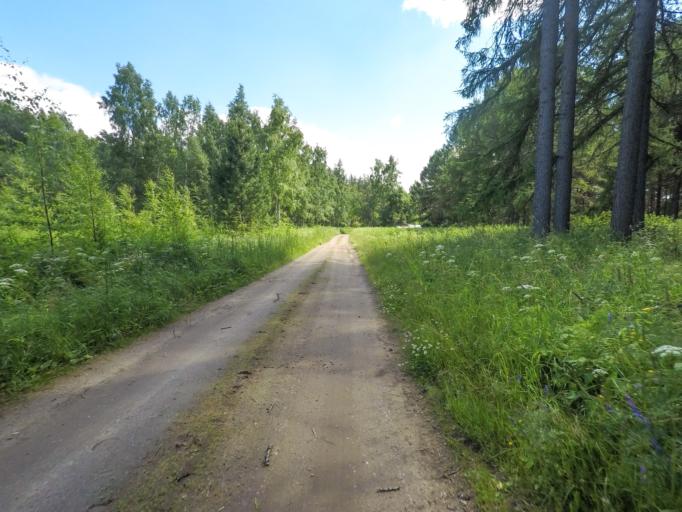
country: FI
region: Southern Savonia
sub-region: Savonlinna
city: Punkaharju
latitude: 61.8078
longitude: 29.3202
